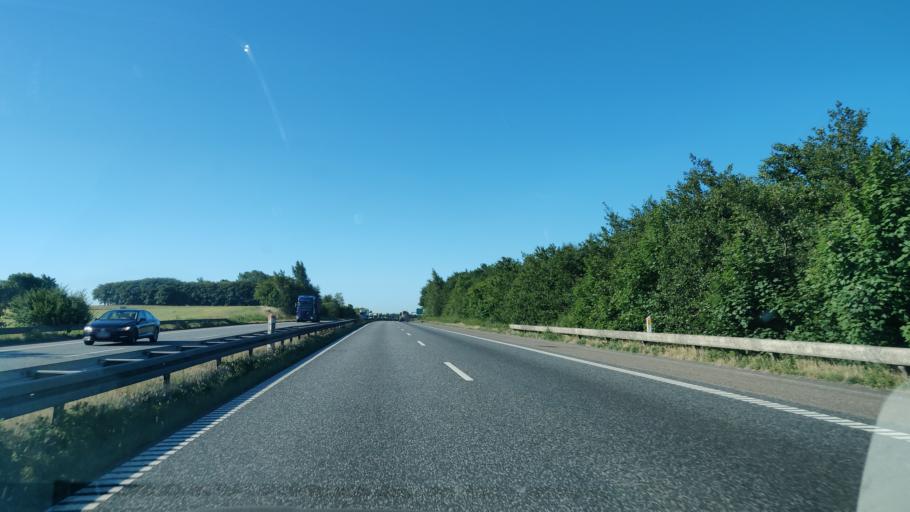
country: DK
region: Central Jutland
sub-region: Arhus Kommune
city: Trige
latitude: 56.2393
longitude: 10.1248
